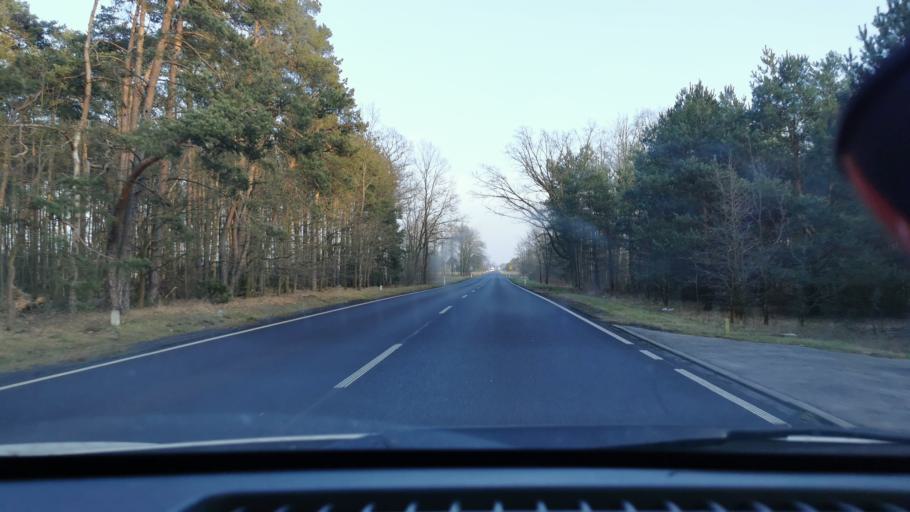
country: PL
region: Lodz Voivodeship
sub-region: Powiat pabianicki
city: Dlutow
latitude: 51.5113
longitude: 19.3580
